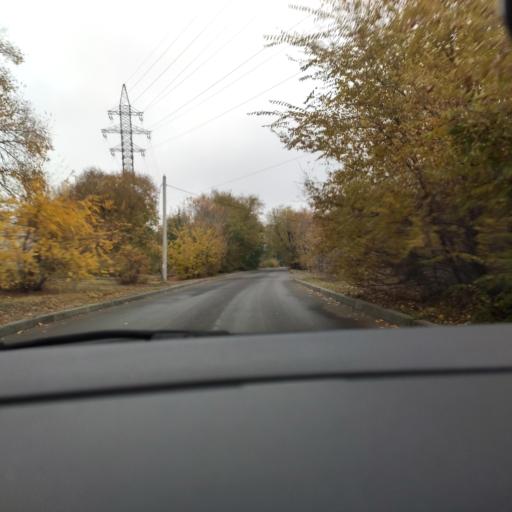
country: RU
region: Voronezj
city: Voronezh
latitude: 51.6345
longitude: 39.2304
